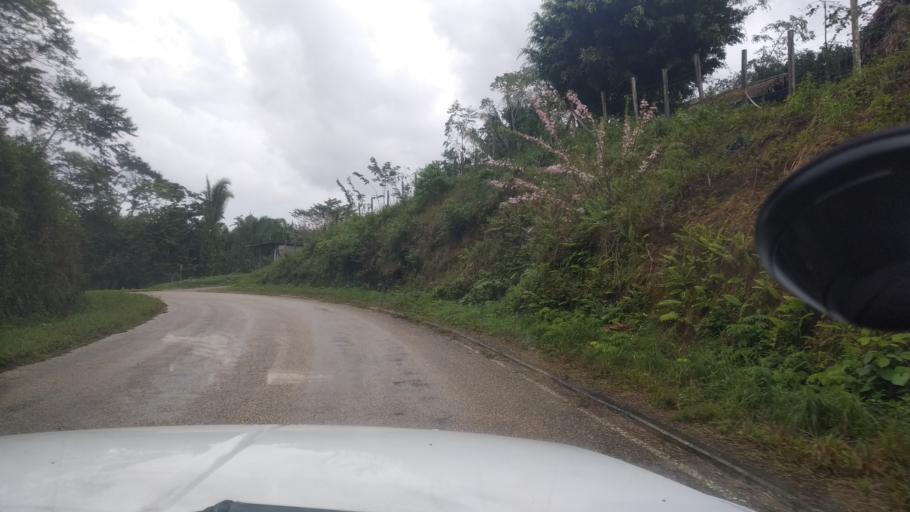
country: GT
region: Peten
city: San Luis
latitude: 16.2017
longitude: -89.1450
